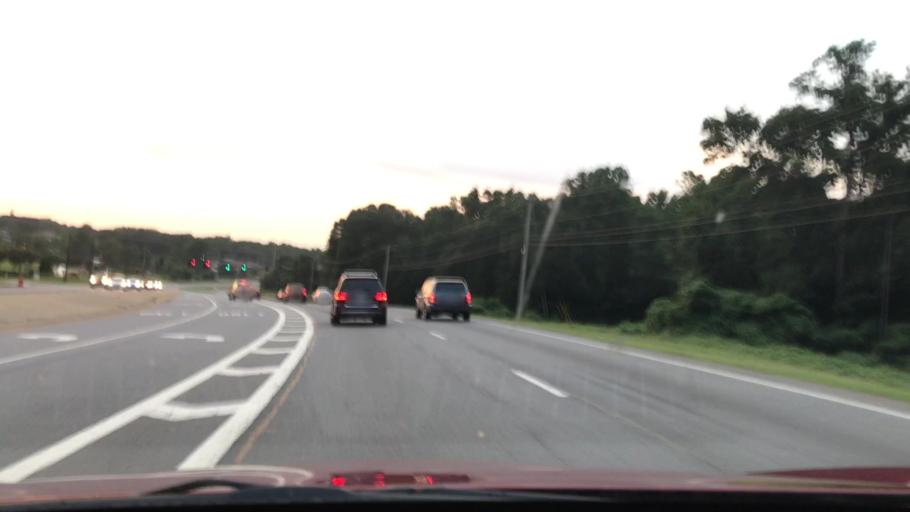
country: US
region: Georgia
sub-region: Gwinnett County
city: Sugar Hill
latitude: 34.0388
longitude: -83.9886
